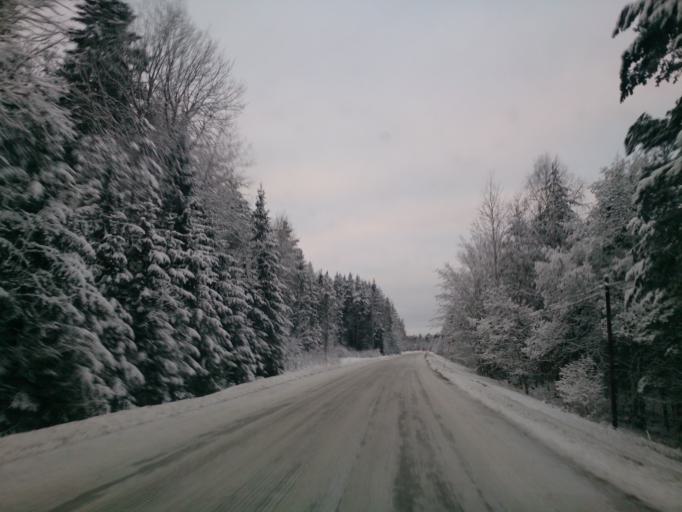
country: SE
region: OEstergoetland
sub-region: Atvidabergs Kommun
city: Atvidaberg
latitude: 58.3209
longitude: 16.0268
